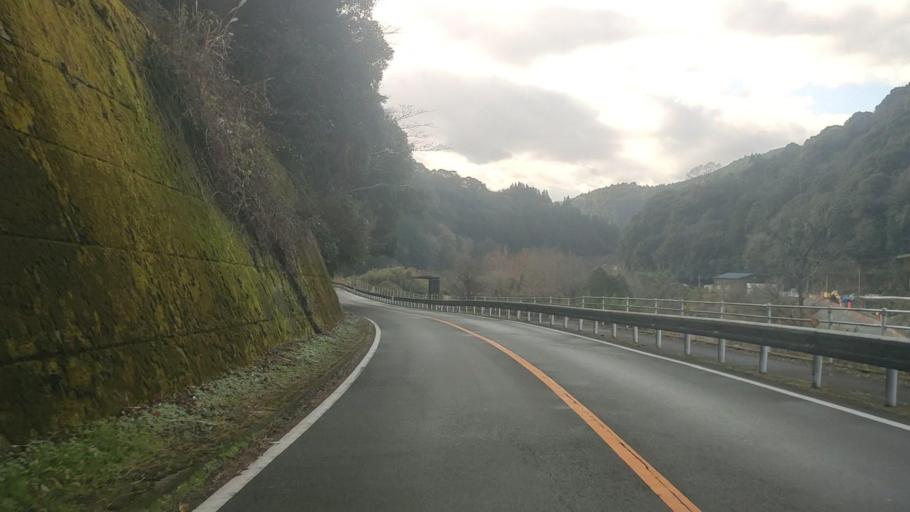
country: JP
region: Kumamoto
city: Hitoyoshi
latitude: 32.2987
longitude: 130.8461
